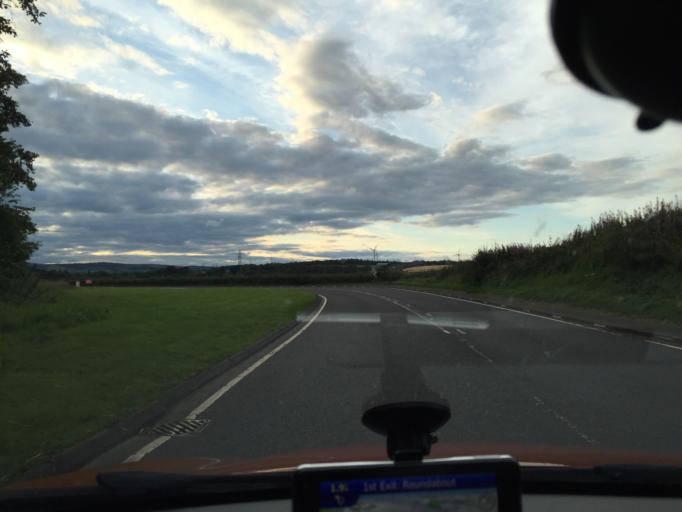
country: GB
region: Scotland
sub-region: Falkirk
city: Larbert
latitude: 56.0088
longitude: -3.8421
